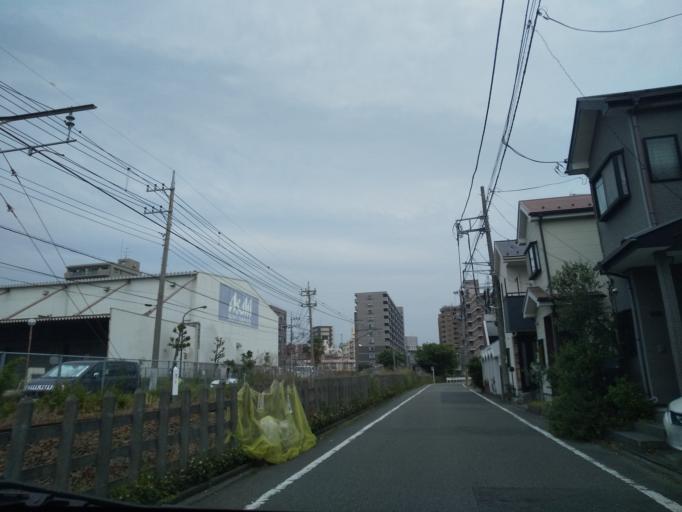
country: JP
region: Tokyo
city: Hachioji
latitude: 35.5777
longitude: 139.3524
